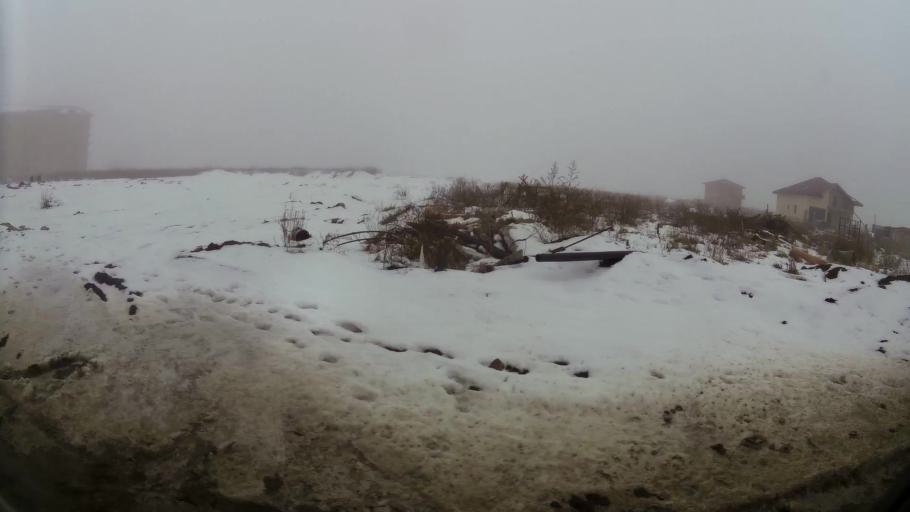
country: RO
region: Ilfov
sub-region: Comuna Chiajna
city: Chiajna
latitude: 44.4474
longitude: 25.9759
